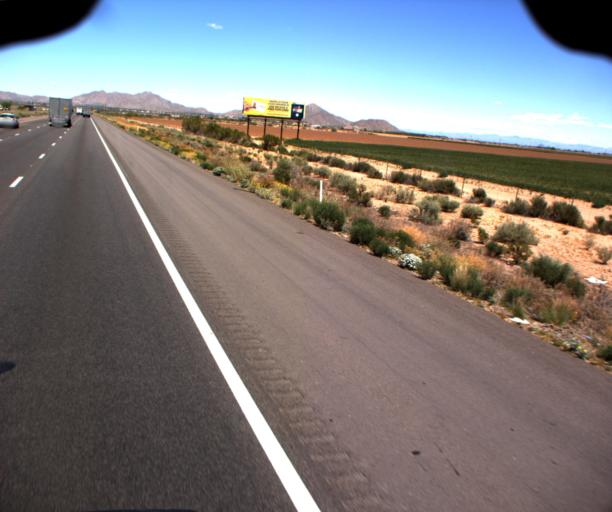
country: US
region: Arizona
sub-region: Pinal County
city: Casa Grande
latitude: 32.9005
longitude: -111.6865
